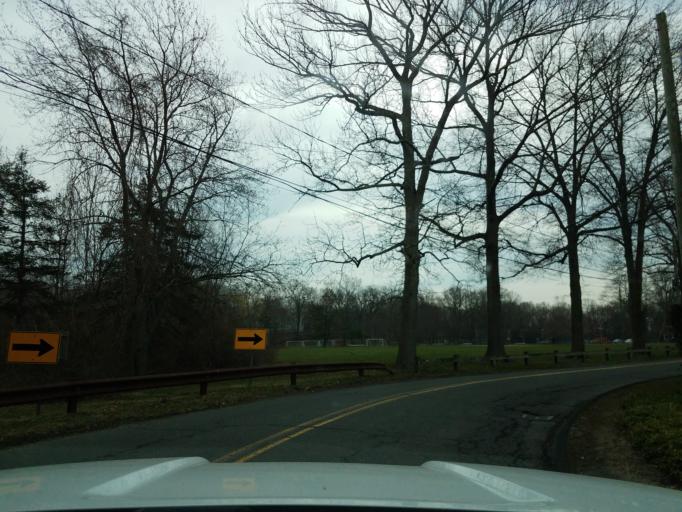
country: US
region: Connecticut
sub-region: Fairfield County
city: Old Greenwich
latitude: 41.0377
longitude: -73.5636
